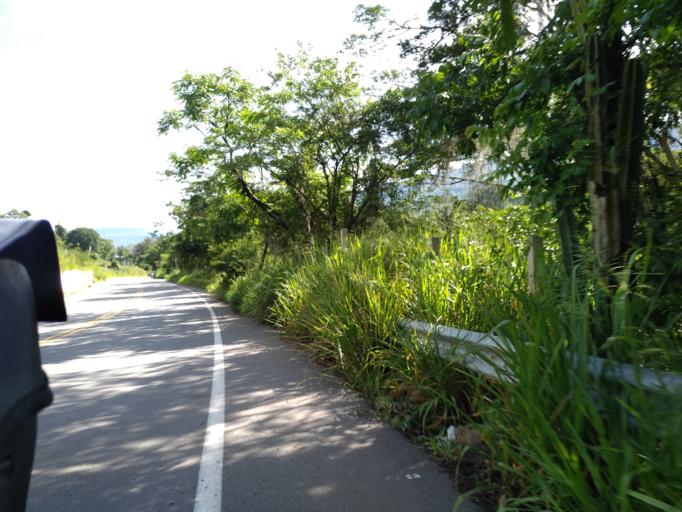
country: CO
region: Santander
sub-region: San Gil
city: San Gil
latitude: 6.5123
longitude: -73.1252
